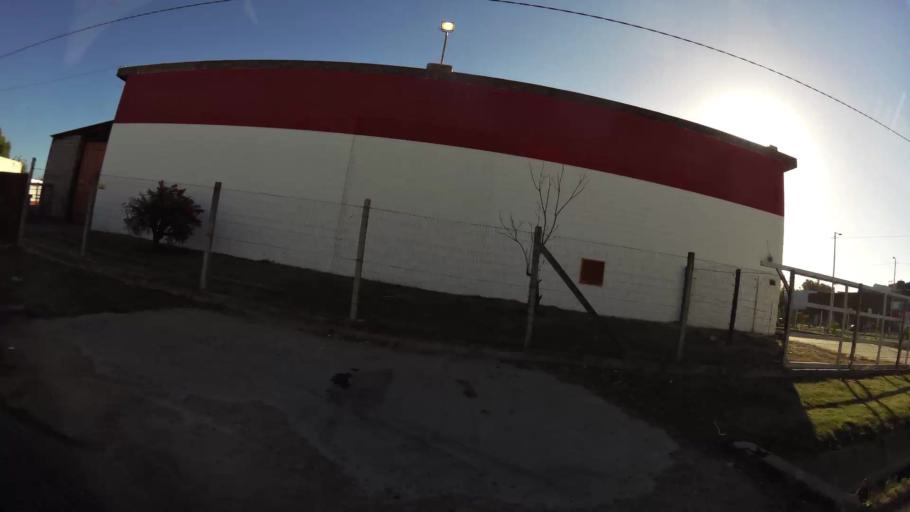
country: UY
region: Canelones
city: Paso de Carrasco
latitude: -34.8650
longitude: -56.0575
